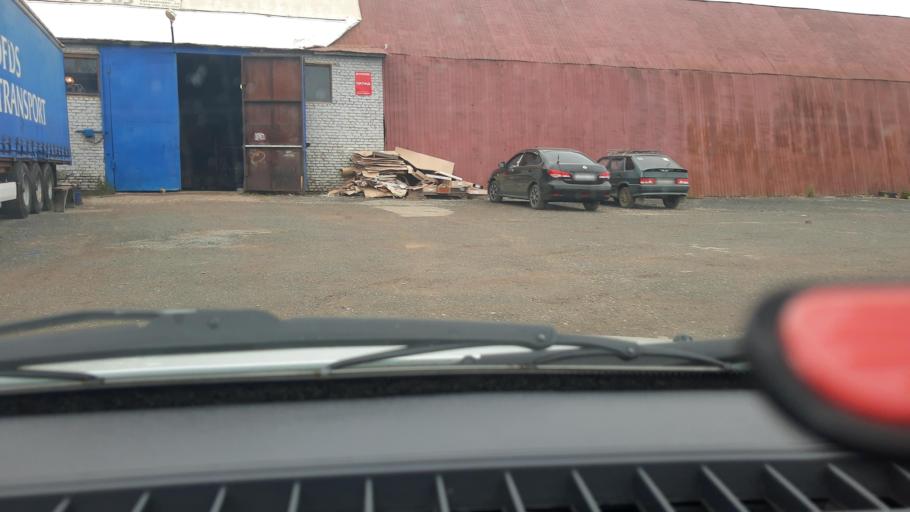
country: RU
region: Bashkortostan
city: Ufa
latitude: 54.7939
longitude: 56.0866
